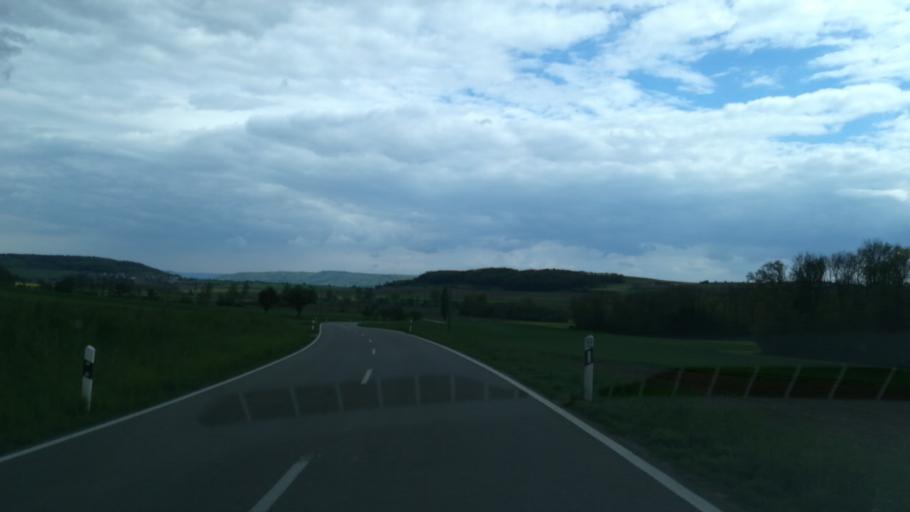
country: CH
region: Schaffhausen
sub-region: Bezirk Reiat
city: Thayngen
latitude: 47.7743
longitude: 8.7253
